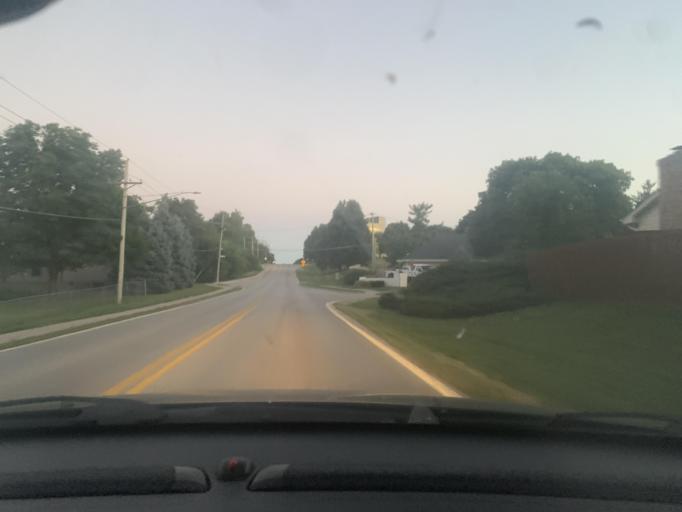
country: US
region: Nebraska
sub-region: Douglas County
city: Ralston
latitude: 41.2742
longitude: -96.0622
